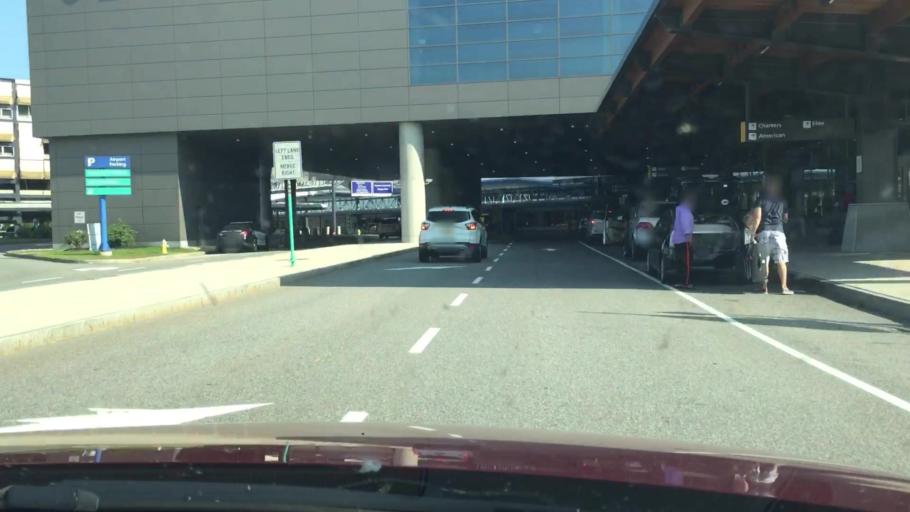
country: US
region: Maine
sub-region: Cumberland County
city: South Portland Gardens
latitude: 43.6483
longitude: -70.3121
